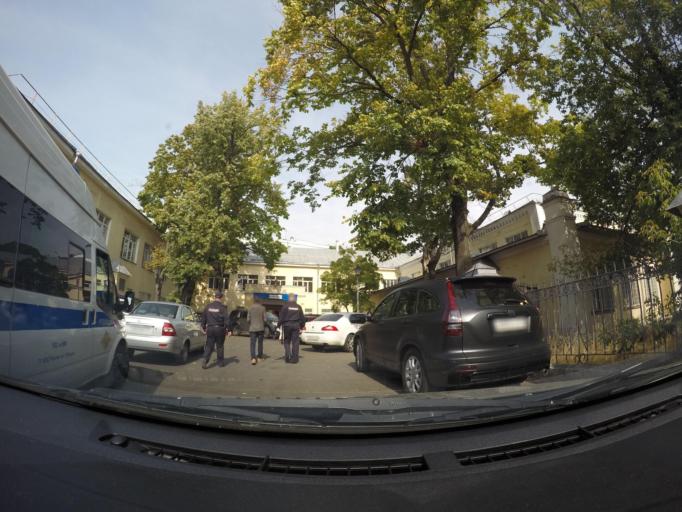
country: RU
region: Moscow
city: Sokol'niki
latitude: 55.7915
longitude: 37.6862
